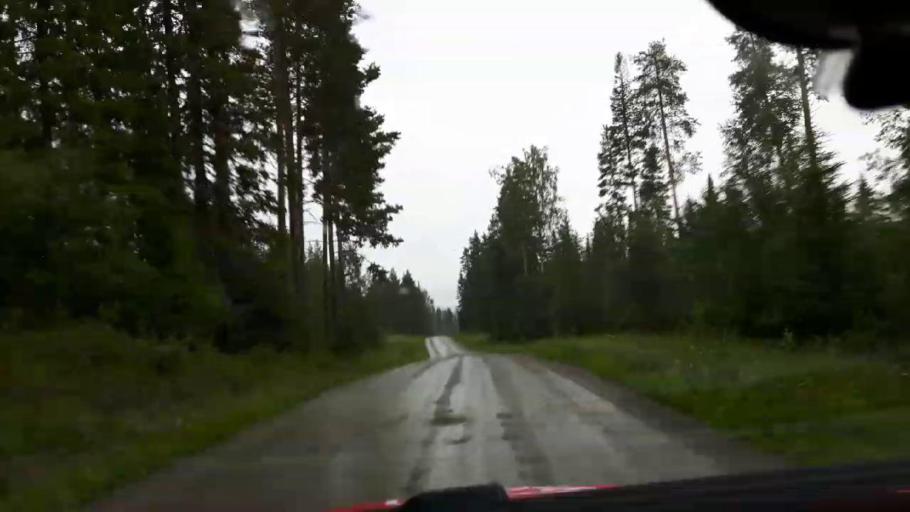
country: SE
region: Jaemtland
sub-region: OEstersunds Kommun
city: Brunflo
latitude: 62.8505
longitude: 14.9684
